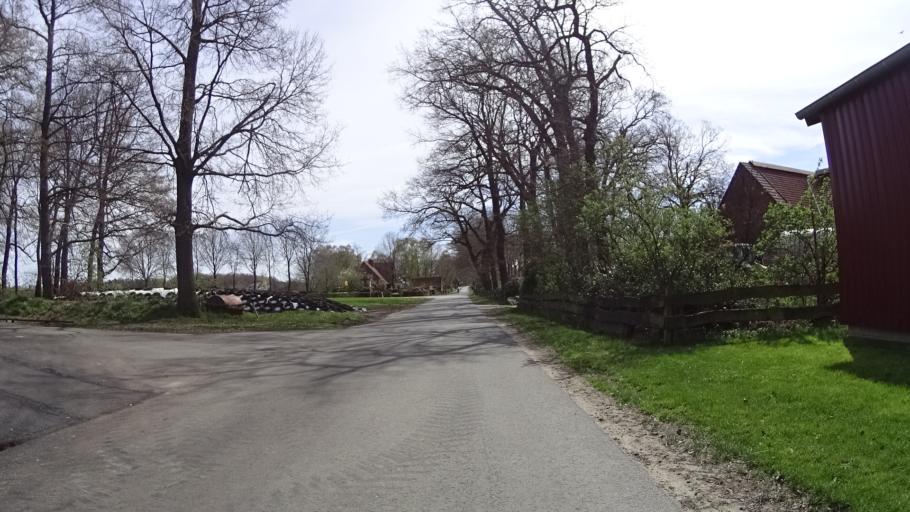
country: DE
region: Lower Saxony
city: Emsburen
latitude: 52.4491
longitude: 7.3372
